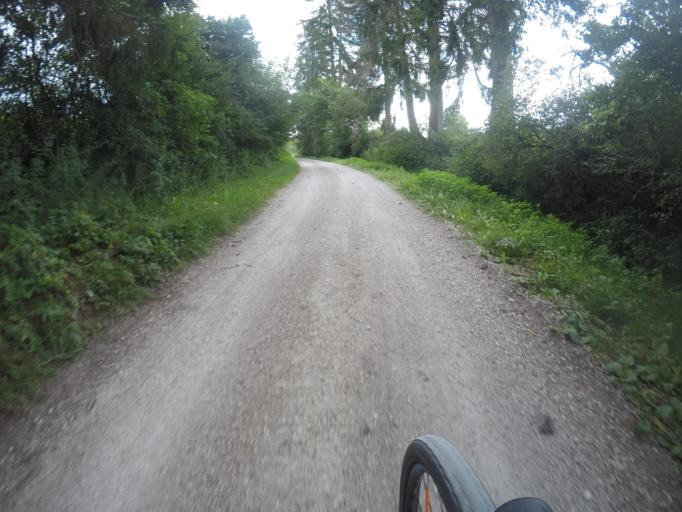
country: DE
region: Baden-Wuerttemberg
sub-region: Tuebingen Region
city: Munsingen
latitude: 48.4349
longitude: 9.4859
